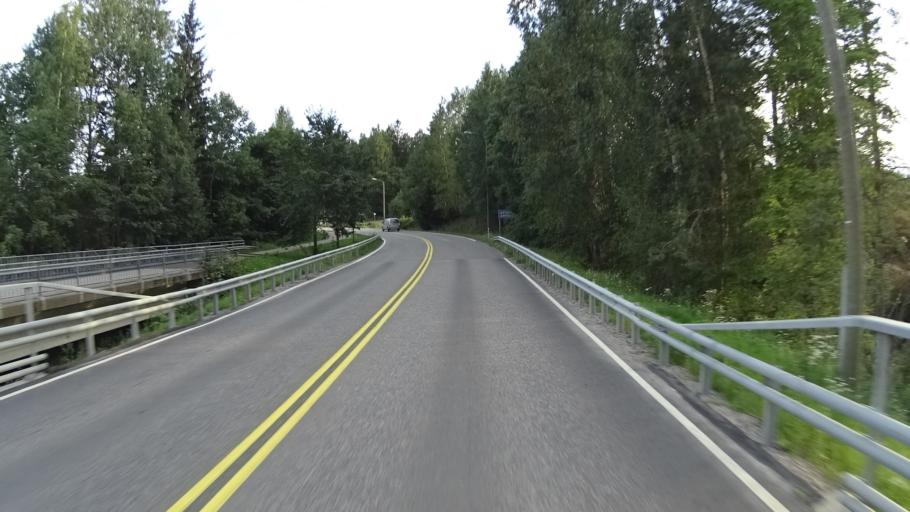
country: FI
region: Uusimaa
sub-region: Helsinki
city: Nurmijaervi
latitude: 60.3438
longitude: 24.8655
